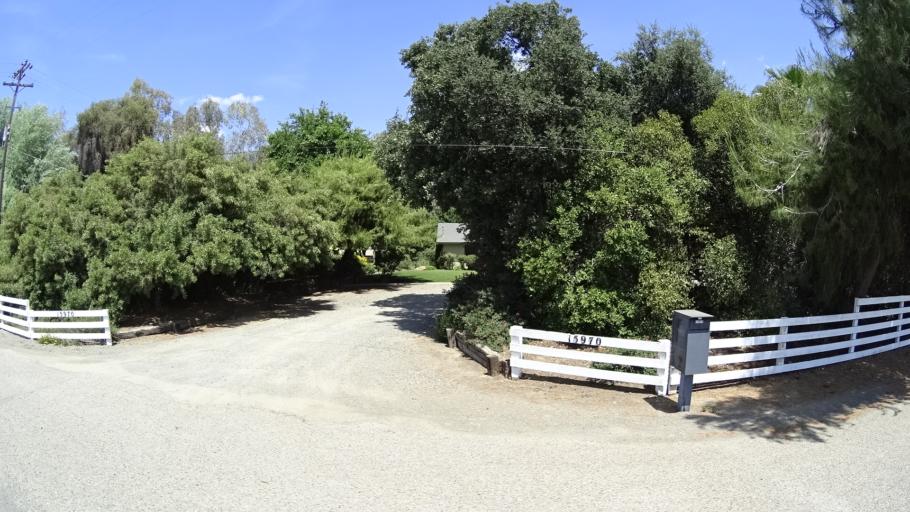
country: US
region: California
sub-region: Kings County
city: Lemoore
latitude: 36.2988
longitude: -119.7440
